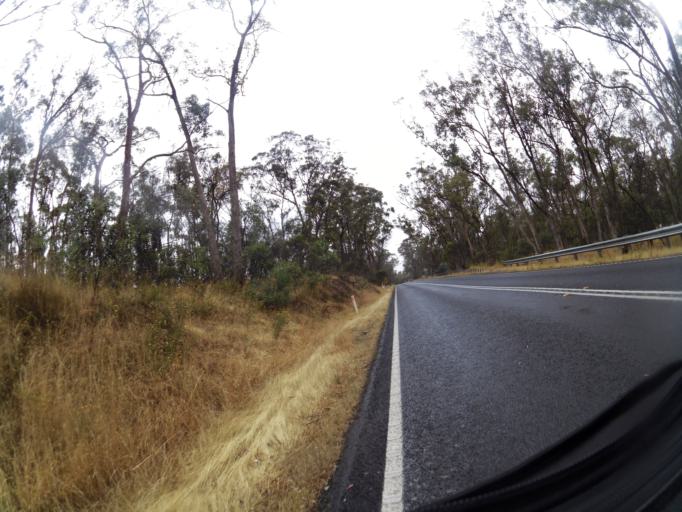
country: AU
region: Victoria
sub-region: Mount Alexander
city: Castlemaine
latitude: -37.1054
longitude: 144.1046
